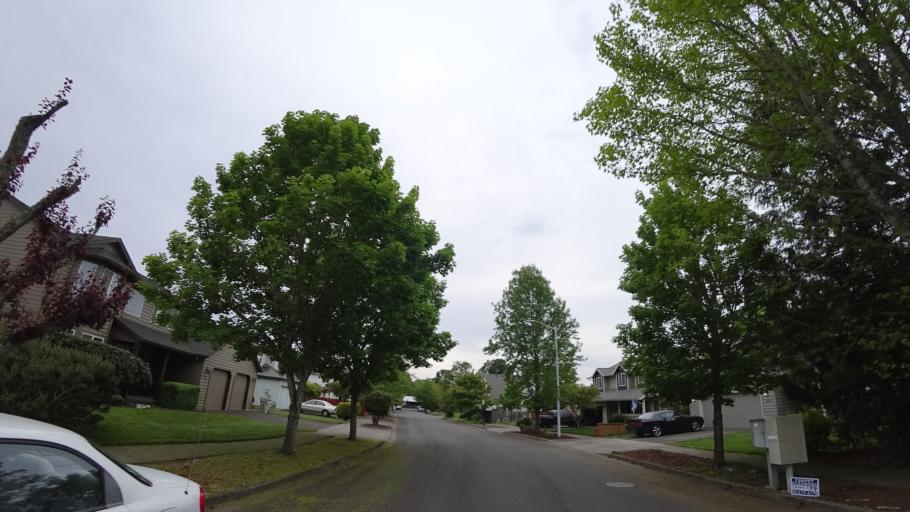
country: US
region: Oregon
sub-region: Washington County
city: Aloha
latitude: 45.5135
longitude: -122.9116
